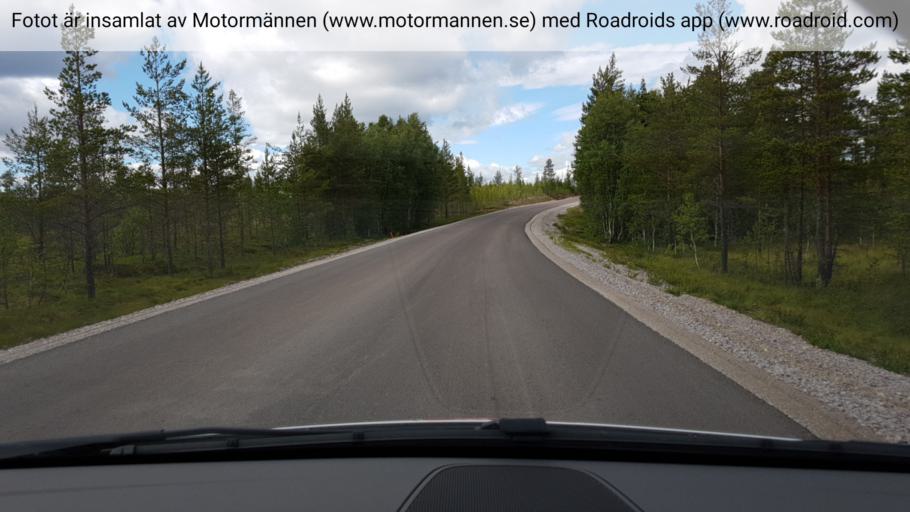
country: SE
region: Jaemtland
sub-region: Harjedalens Kommun
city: Sveg
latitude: 61.7099
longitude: 14.1698
